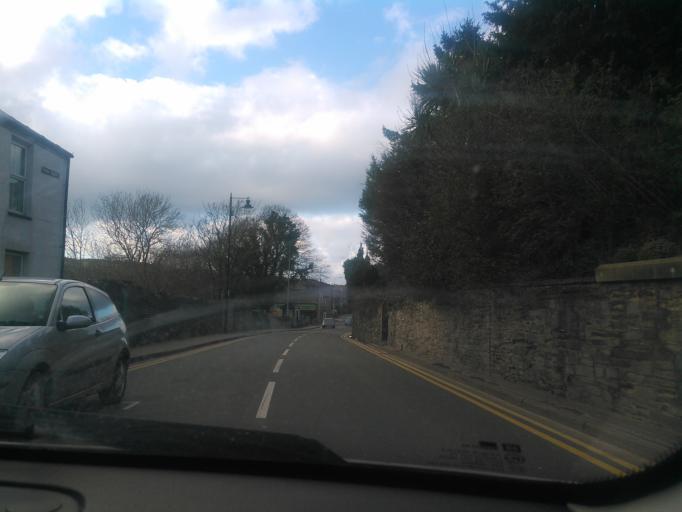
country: GB
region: Wales
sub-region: Gwynedd
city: Bethesda
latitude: 53.1809
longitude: -4.0645
